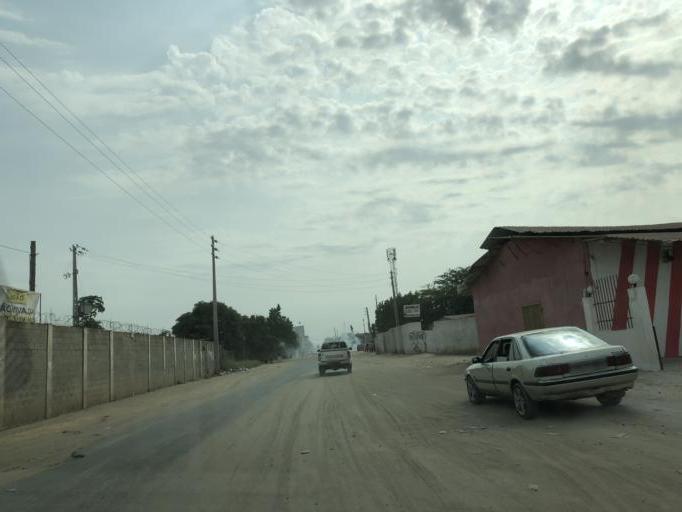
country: AO
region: Luanda
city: Luanda
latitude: -8.9049
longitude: 13.3450
